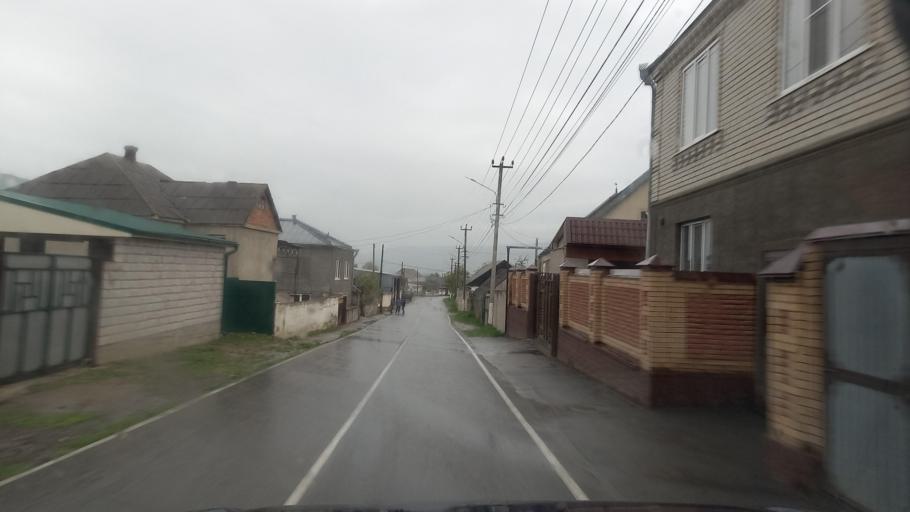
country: RU
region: Kabardino-Balkariya
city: Gundelen
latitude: 43.5950
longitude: 43.1759
